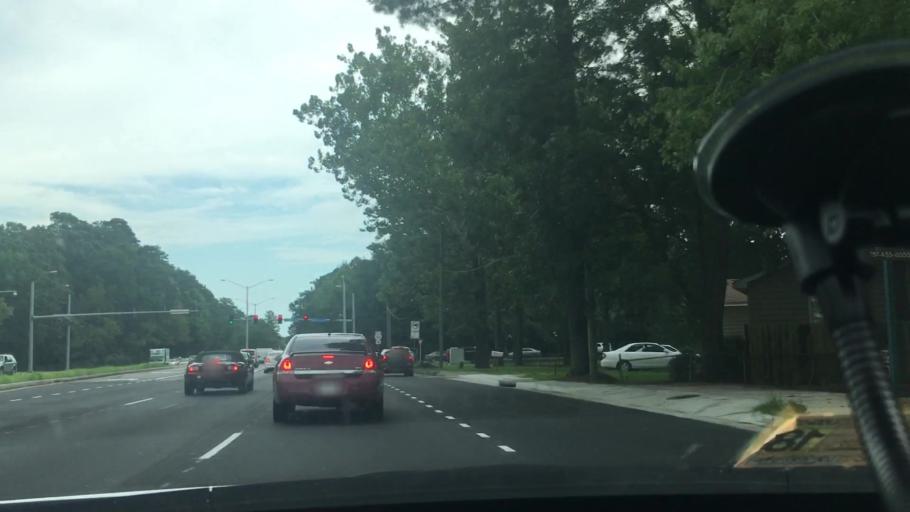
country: US
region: Virginia
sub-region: City of Norfolk
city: Norfolk
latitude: 36.8743
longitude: -76.2077
